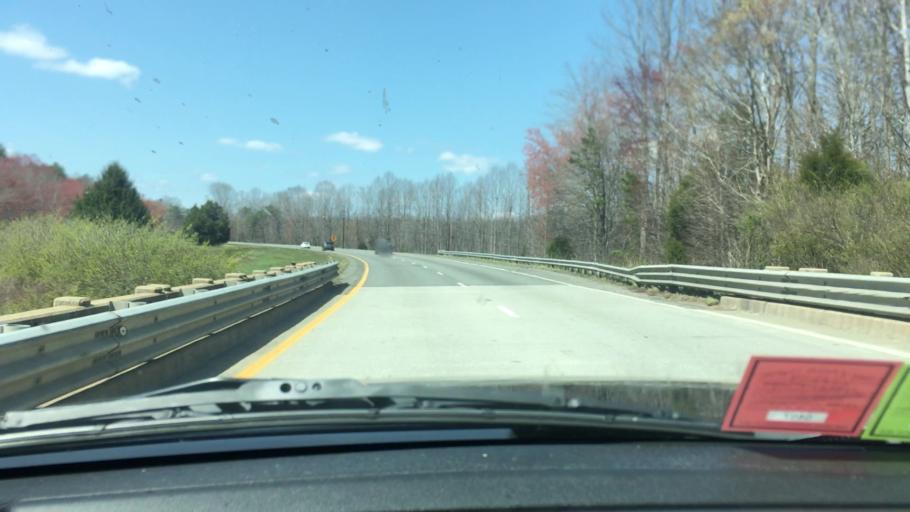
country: US
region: North Carolina
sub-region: Surry County
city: Pilot Mountain
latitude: 36.3996
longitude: -80.4917
